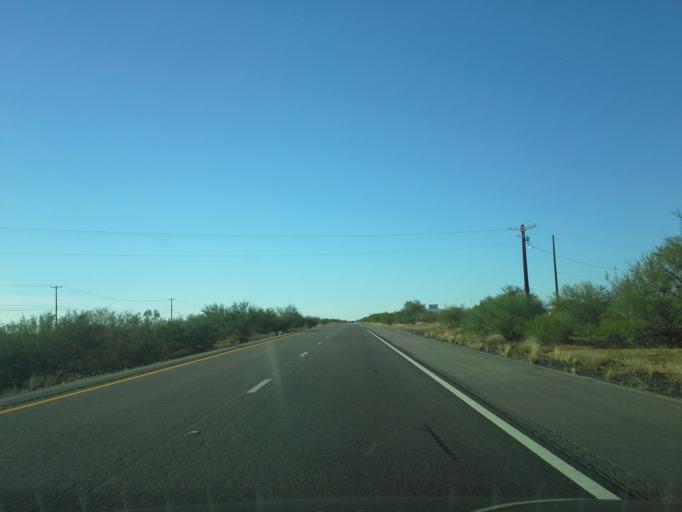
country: US
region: Arizona
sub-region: Pinal County
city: Gold Camp
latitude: 33.3001
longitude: -111.3962
